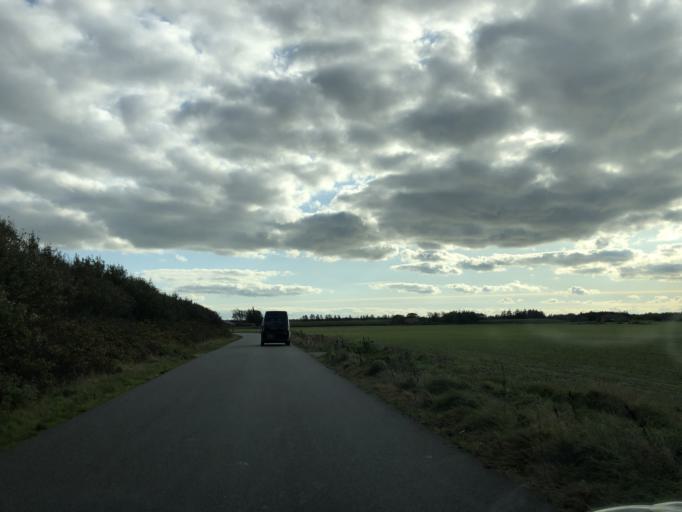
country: DK
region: Central Jutland
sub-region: Holstebro Kommune
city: Ulfborg
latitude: 56.3232
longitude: 8.1572
